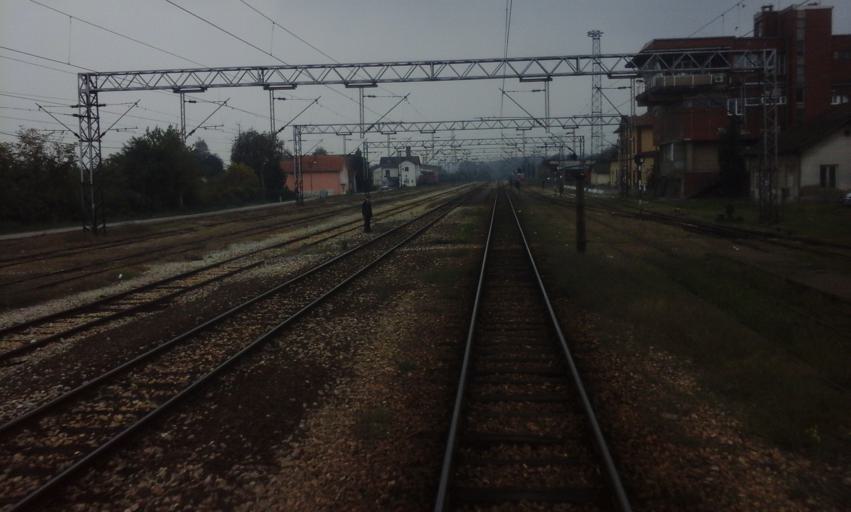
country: RS
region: Central Serbia
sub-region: Sumadijski Okrug
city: Batocina
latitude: 44.1589
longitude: 21.1015
